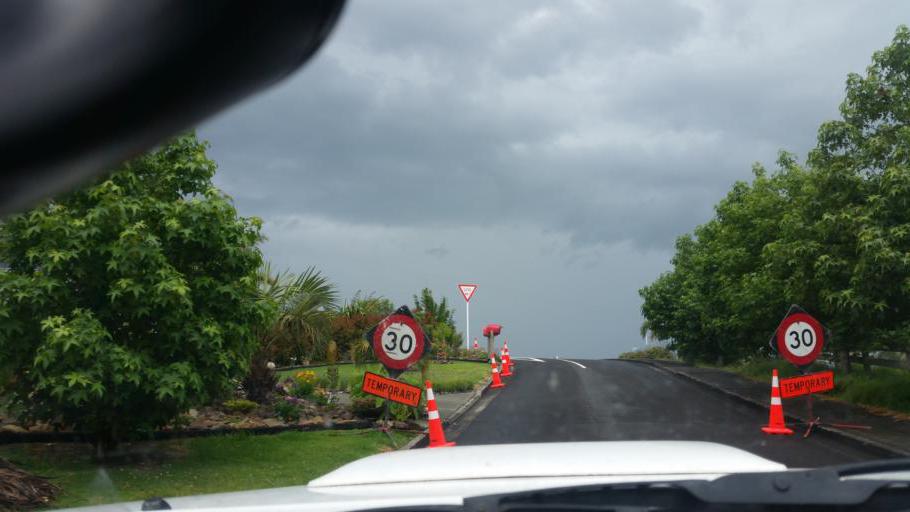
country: NZ
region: Auckland
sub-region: Auckland
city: Wellsford
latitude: -36.1526
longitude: 174.2231
